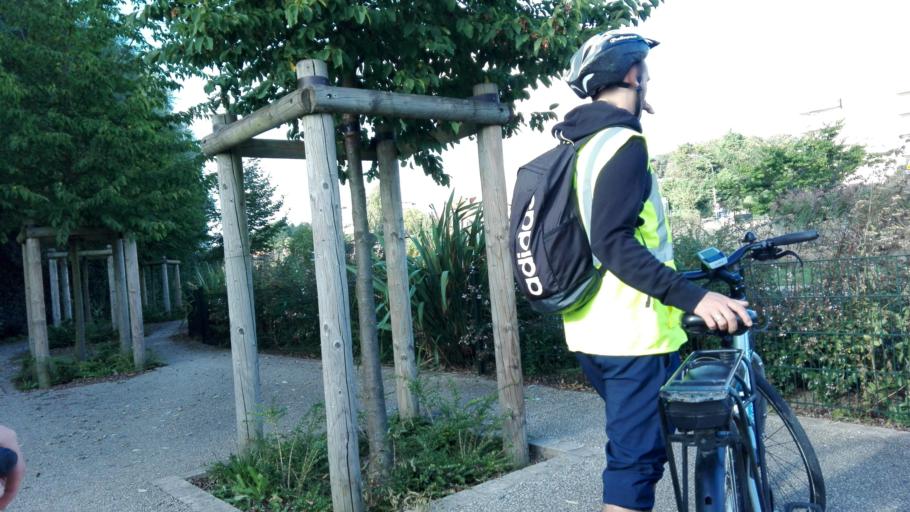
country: FR
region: Nord-Pas-de-Calais
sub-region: Departement du Pas-de-Calais
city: Boulogne-sur-Mer
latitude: 50.7052
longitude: 1.6133
